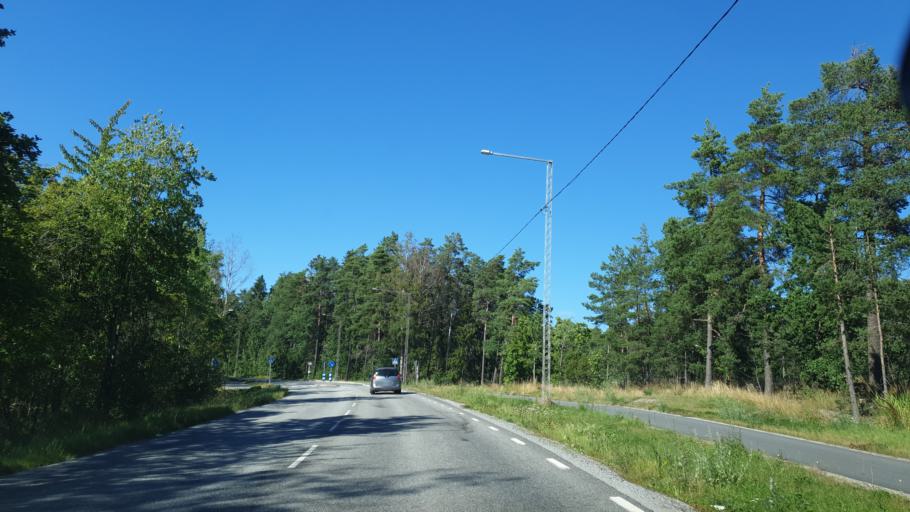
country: SE
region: Stockholm
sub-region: Jarfalla Kommun
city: Jakobsberg
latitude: 59.4359
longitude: 17.8434
